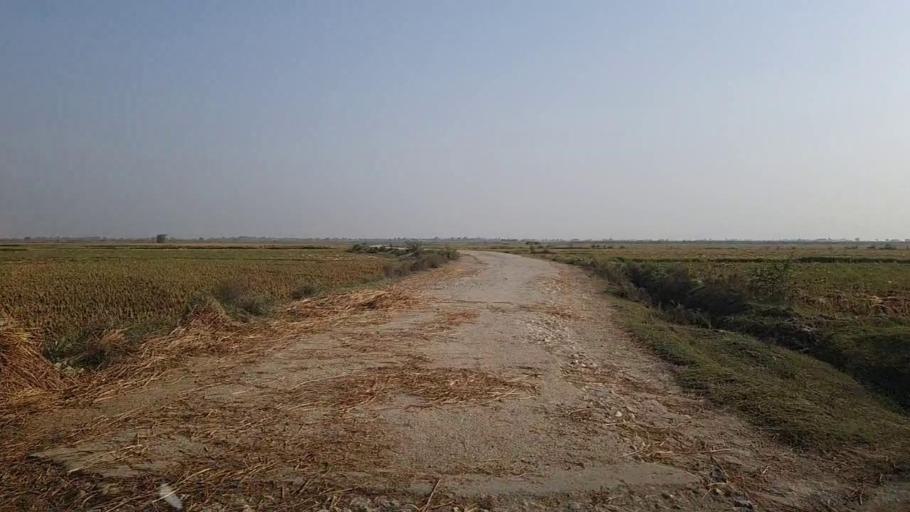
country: PK
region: Sindh
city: Kandhkot
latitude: 28.3014
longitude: 69.2502
